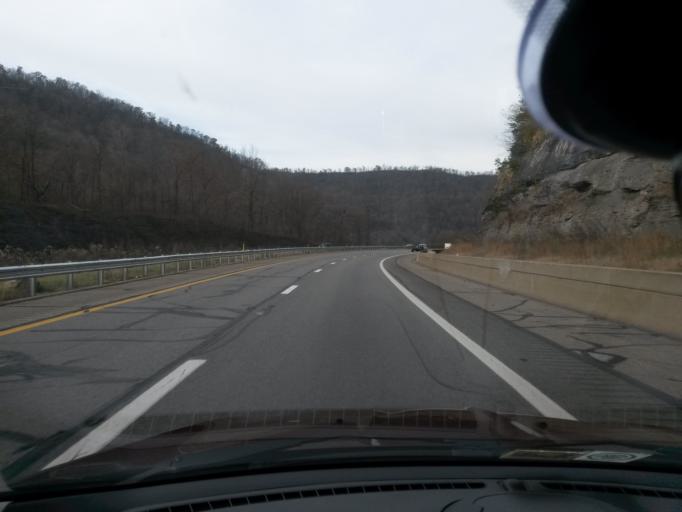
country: US
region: West Virginia
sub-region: Kanawha County
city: Chesapeake
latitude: 38.1744
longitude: -81.4497
